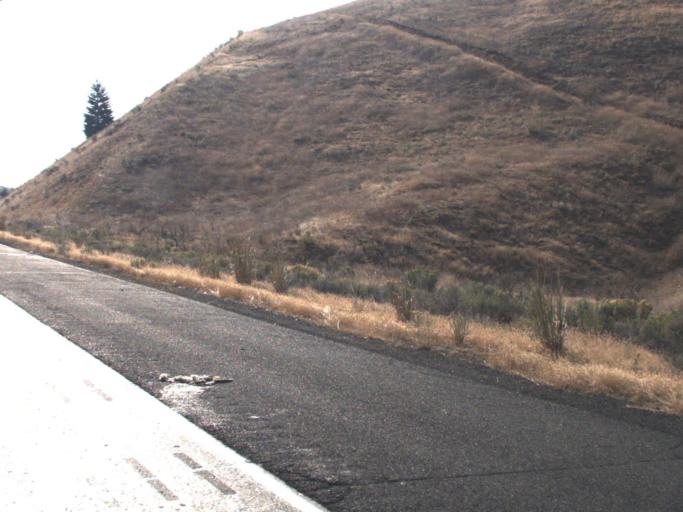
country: US
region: Washington
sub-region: Kittitas County
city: Kittitas
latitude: 46.8914
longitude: -120.4377
